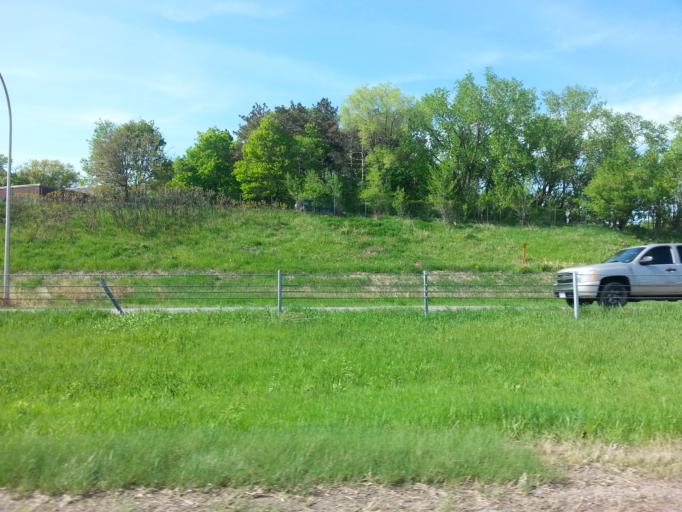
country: US
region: Minnesota
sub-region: Ramsey County
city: Little Canada
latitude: 45.0080
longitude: -93.1001
